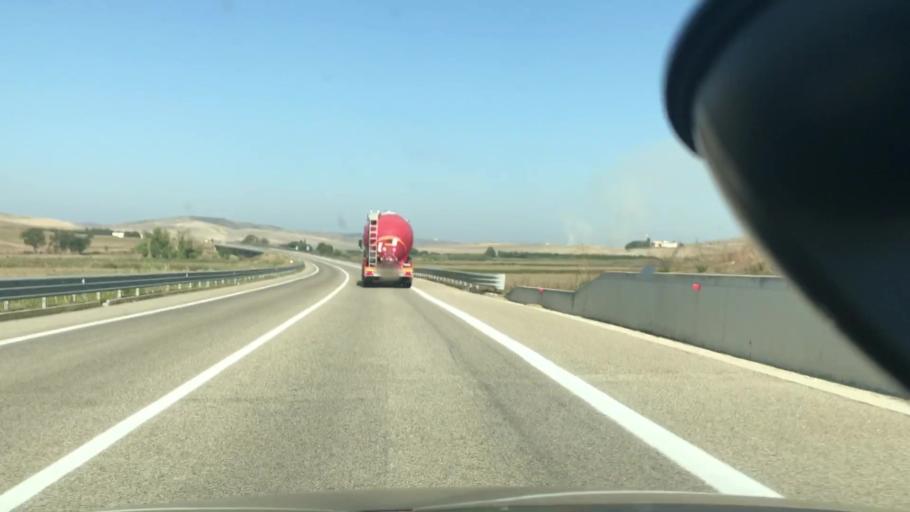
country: IT
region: Basilicate
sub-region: Provincia di Matera
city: Irsina
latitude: 40.7804
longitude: 16.3148
